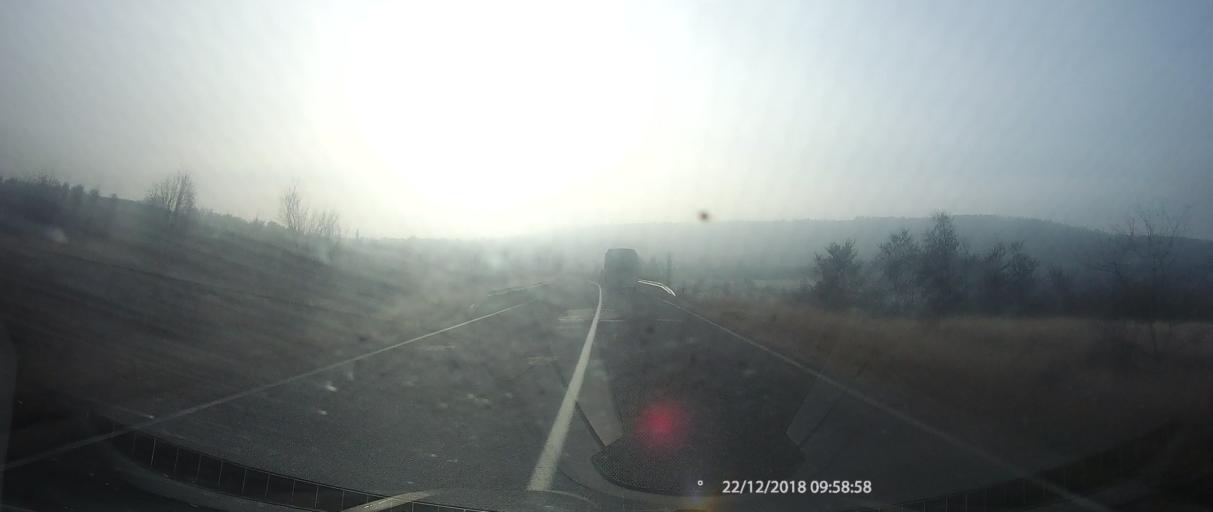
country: MK
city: Klechovce
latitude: 42.1543
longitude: 21.9514
